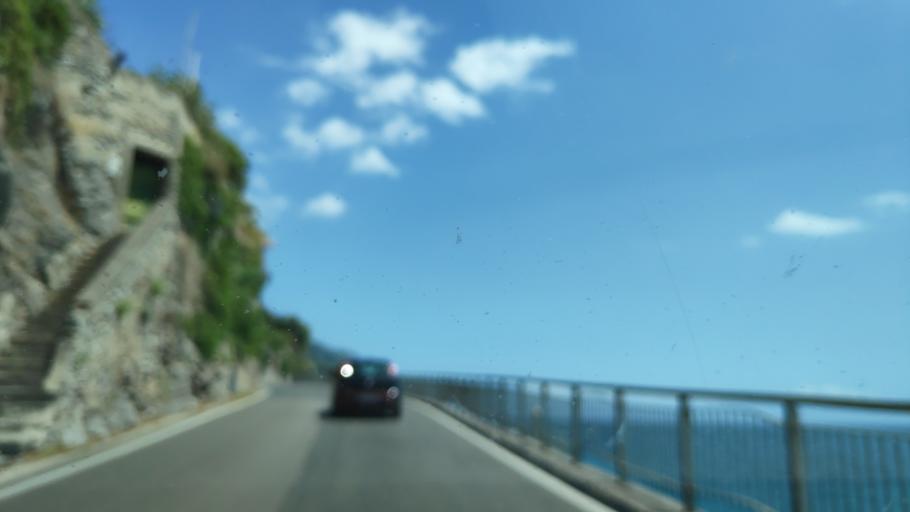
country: IT
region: Campania
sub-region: Provincia di Salerno
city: Minori
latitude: 40.6484
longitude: 14.6303
